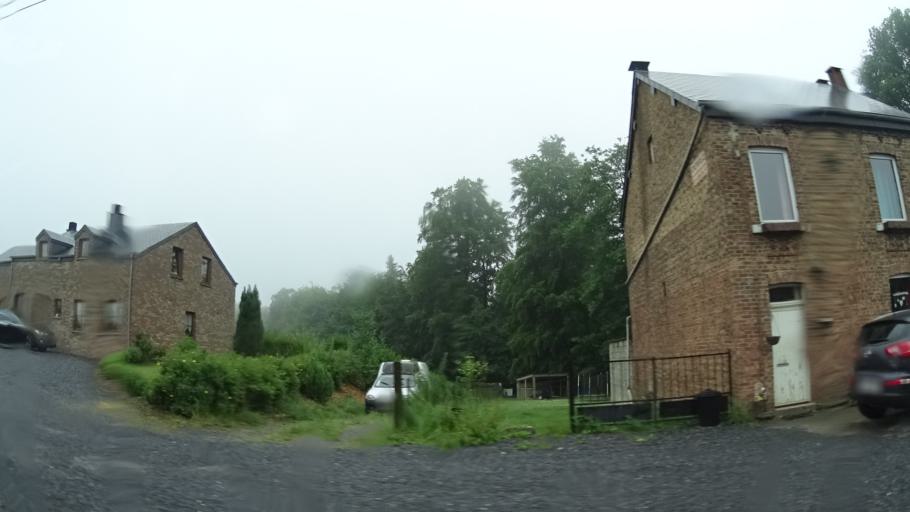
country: BE
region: Wallonia
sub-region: Province de Namur
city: Bievre
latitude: 50.0001
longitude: 5.0060
